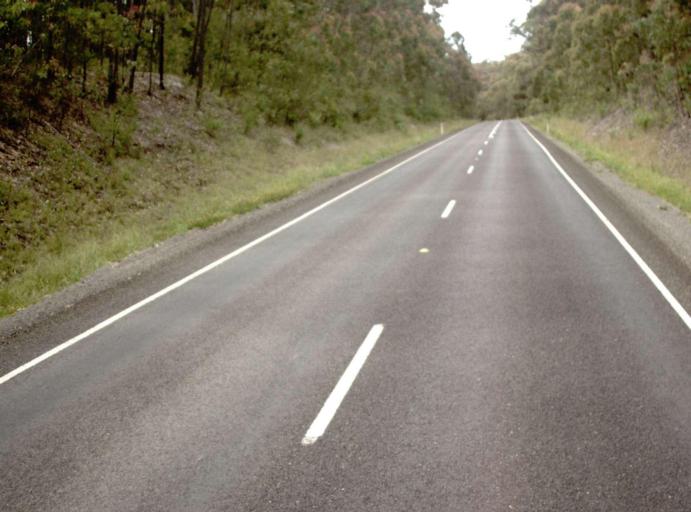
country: AU
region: Victoria
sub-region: Latrobe
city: Traralgon
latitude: -38.1016
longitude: 146.4433
